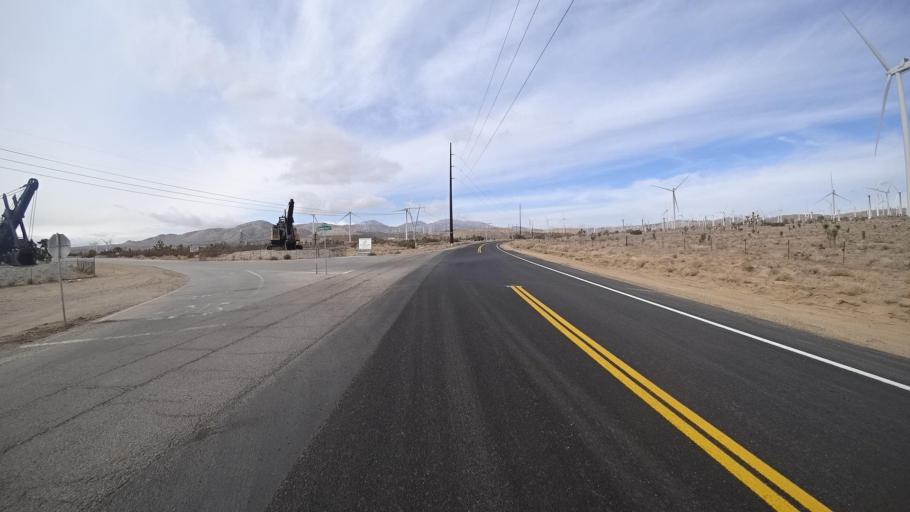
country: US
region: California
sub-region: Kern County
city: Mojave
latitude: 35.0384
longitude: -118.2975
